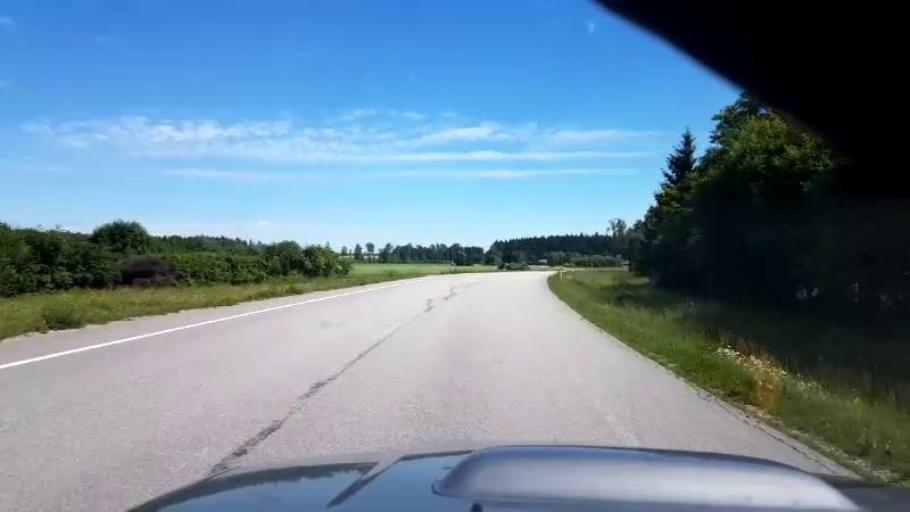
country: EE
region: Jaervamaa
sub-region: Koeru vald
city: Koeru
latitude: 58.9847
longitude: 26.0368
